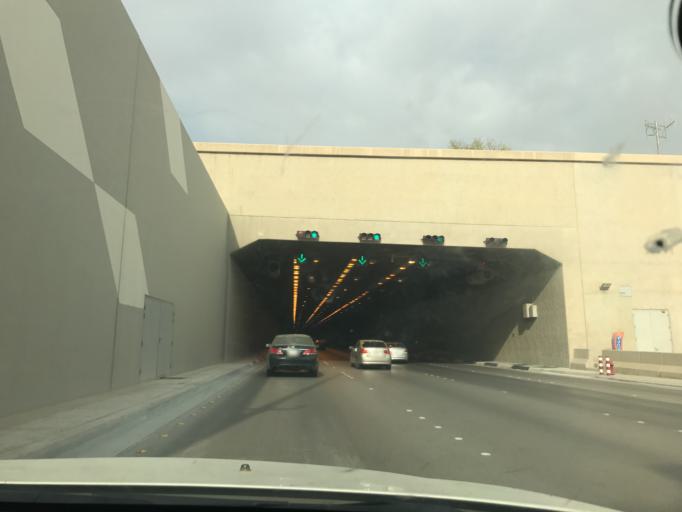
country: SA
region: Ar Riyad
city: Riyadh
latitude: 24.7275
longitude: 46.7118
